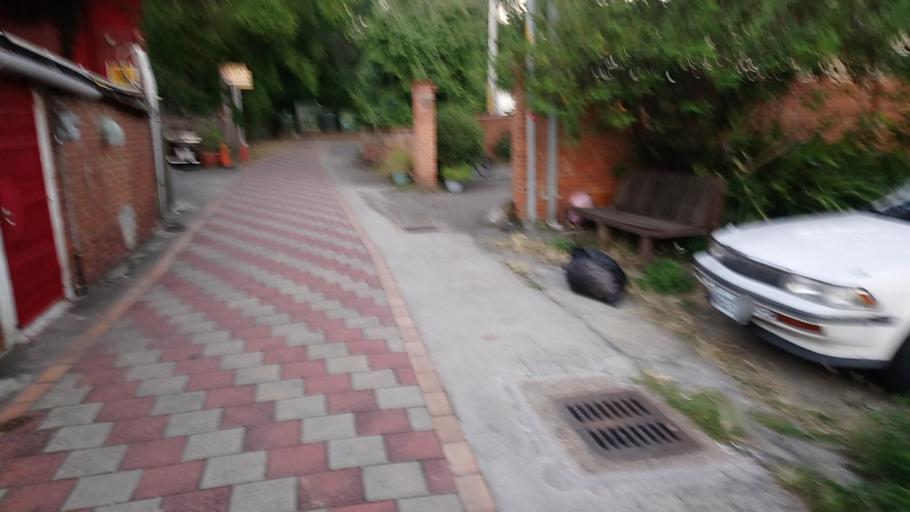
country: TW
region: Taiwan
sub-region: Miaoli
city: Miaoli
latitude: 24.6773
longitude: 120.8900
